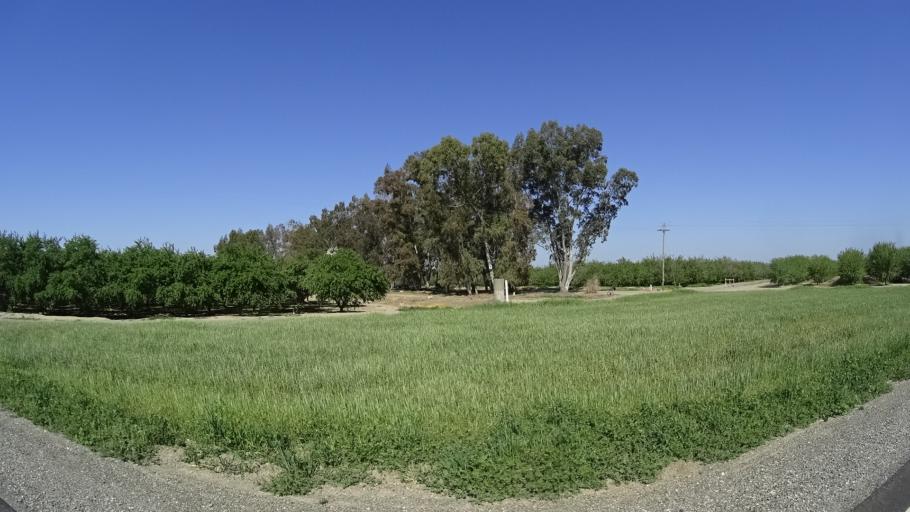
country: US
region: California
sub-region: Glenn County
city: Hamilton City
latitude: 39.6591
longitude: -122.0645
